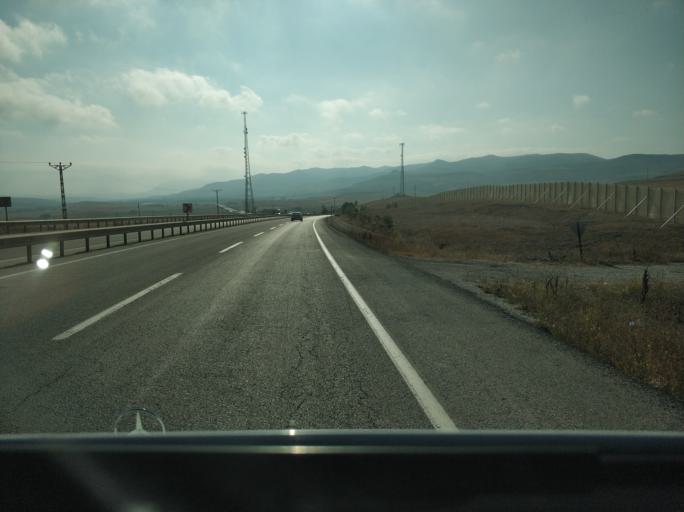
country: TR
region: Sivas
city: Yildizeli
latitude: 39.8350
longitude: 36.4113
